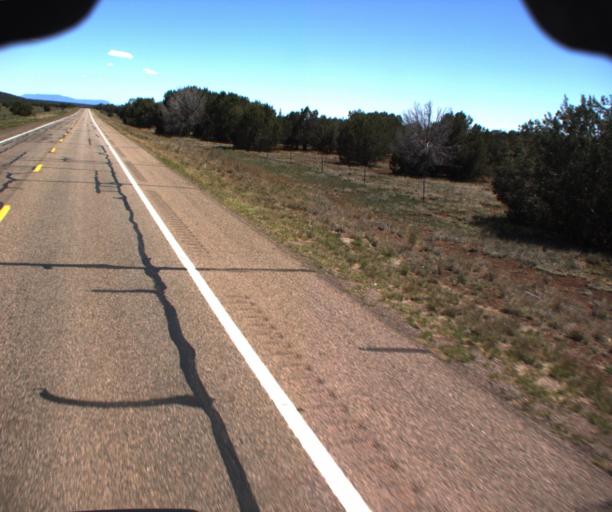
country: US
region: Arizona
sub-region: Yavapai County
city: Paulden
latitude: 35.1576
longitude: -112.4542
